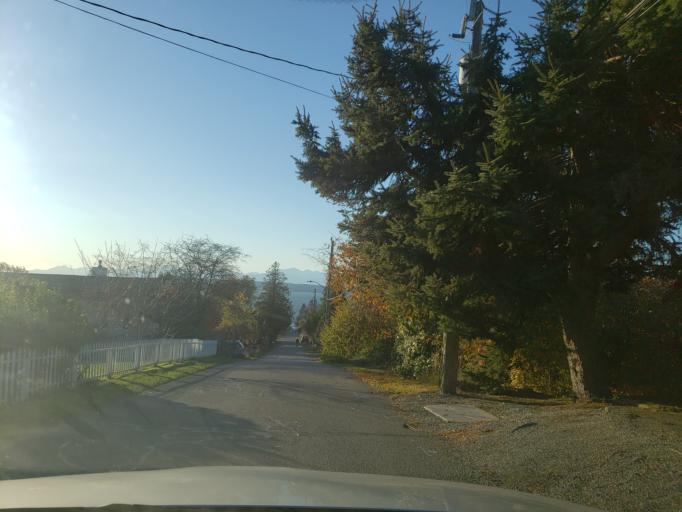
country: US
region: Washington
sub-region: Snohomish County
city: Woodway
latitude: 47.7738
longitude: -122.3859
